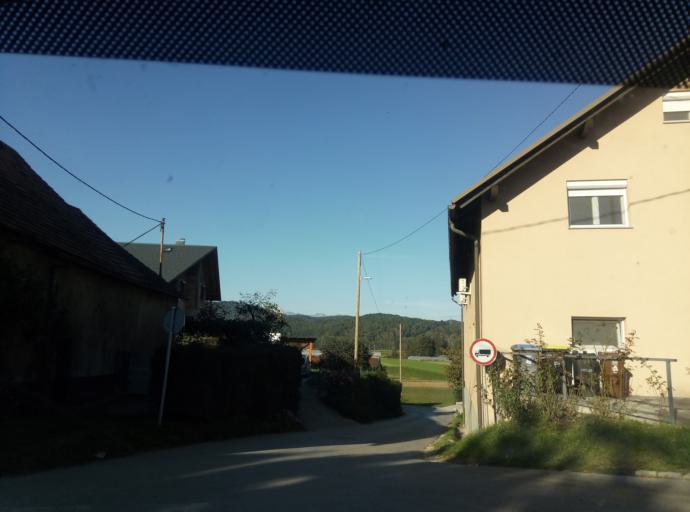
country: SI
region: Ljubljana
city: Ljubljana
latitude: 46.0954
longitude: 14.5031
